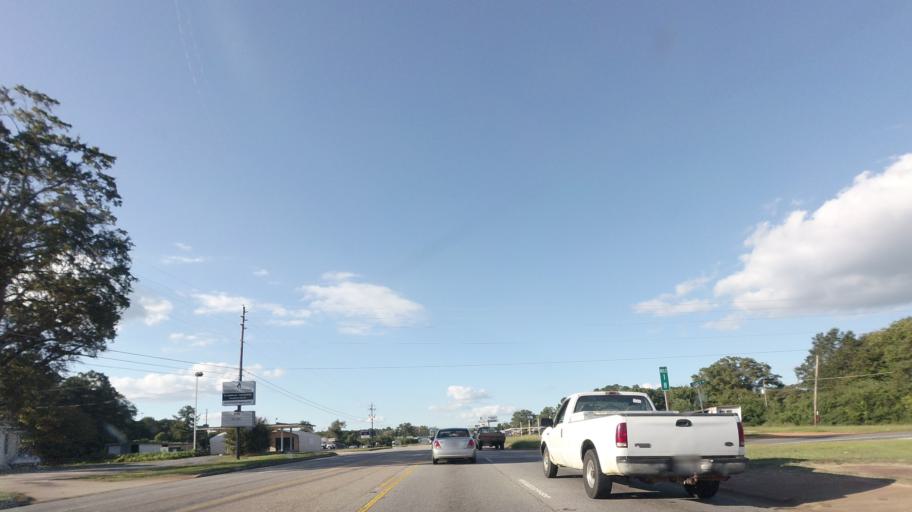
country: US
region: Georgia
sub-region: Upson County
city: Hannahs Mill
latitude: 32.9309
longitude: -84.3340
